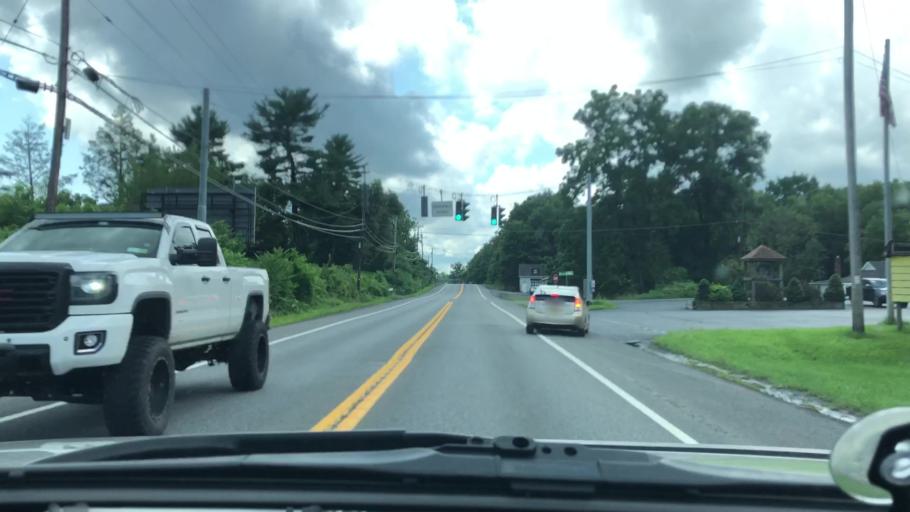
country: US
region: New York
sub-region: Ulster County
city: Saugerties
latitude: 42.0958
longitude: -73.9720
